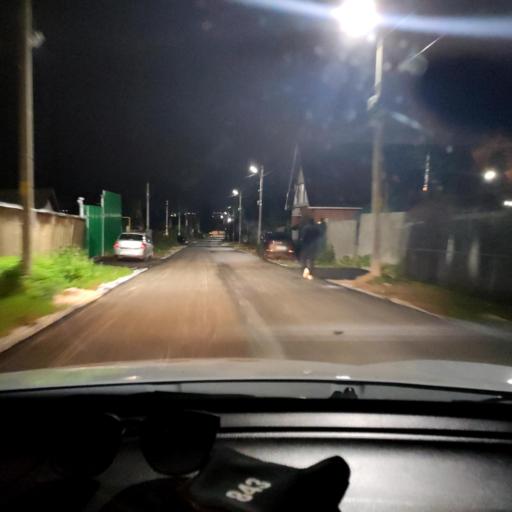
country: RU
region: Tatarstan
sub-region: Gorod Kazan'
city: Kazan
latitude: 55.7394
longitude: 49.1685
